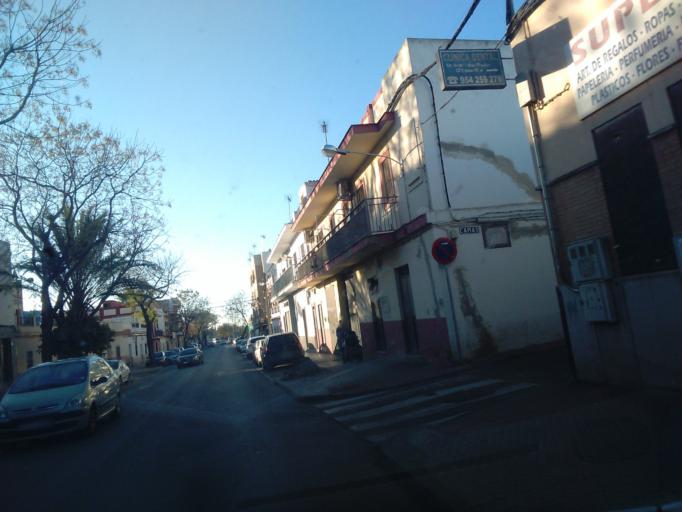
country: ES
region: Andalusia
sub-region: Provincia de Sevilla
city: Sevilla
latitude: 37.3859
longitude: -5.9108
